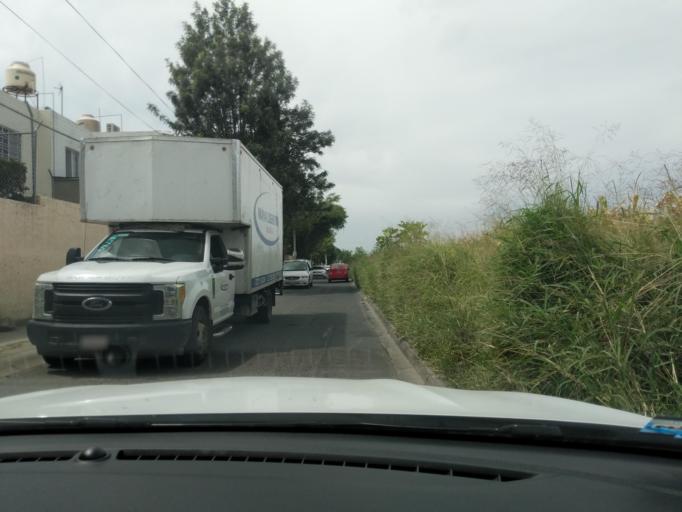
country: MX
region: Jalisco
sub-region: Zapopan
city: La Cuchilla (Extramuros de Tesistan)
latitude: 20.7805
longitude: -103.4647
